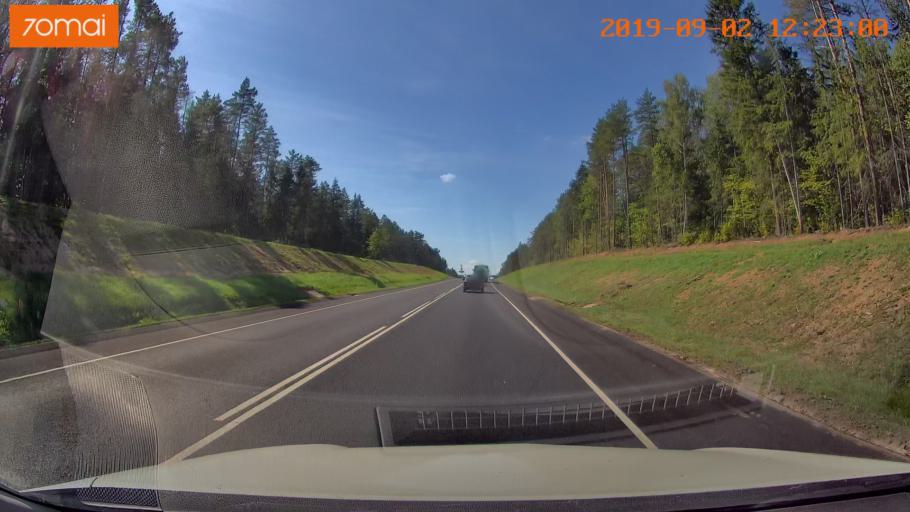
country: RU
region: Smolensk
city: Shumyachi
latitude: 53.8773
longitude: 32.6256
